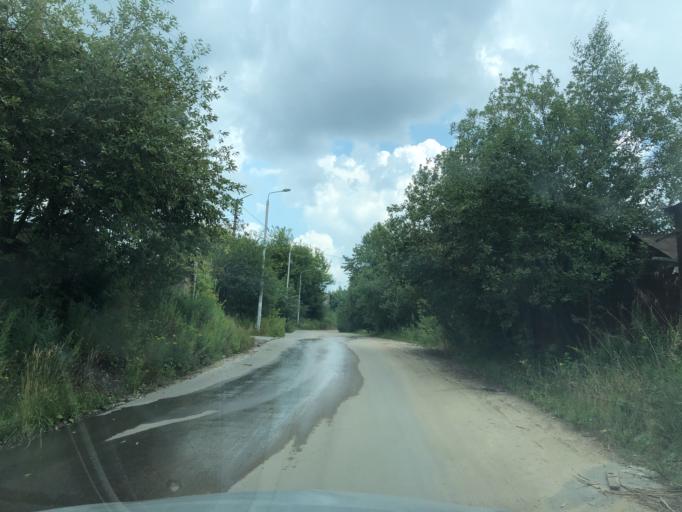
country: RU
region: Tula
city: Mendeleyevskiy
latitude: 54.1588
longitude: 37.5795
